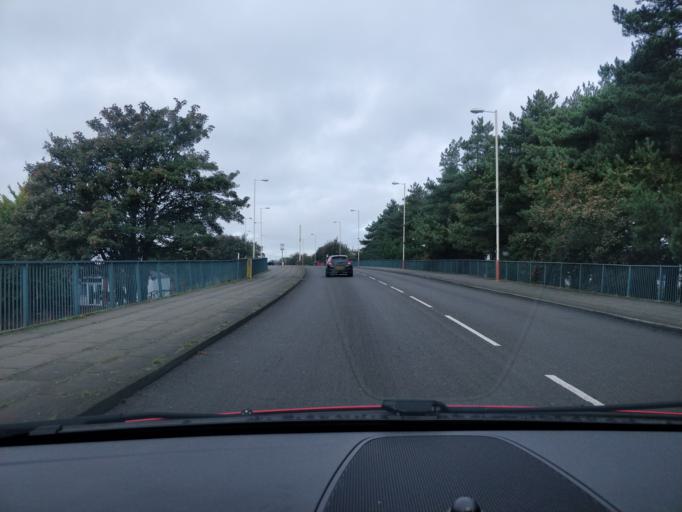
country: GB
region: England
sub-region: Sefton
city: Southport
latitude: 53.6212
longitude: -3.0237
